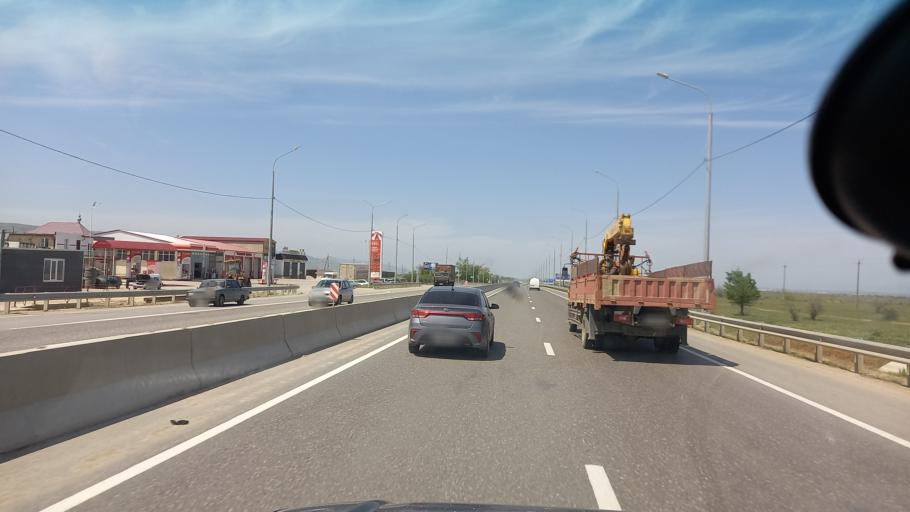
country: RU
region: Dagestan
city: Manas
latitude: 42.7315
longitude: 47.6646
